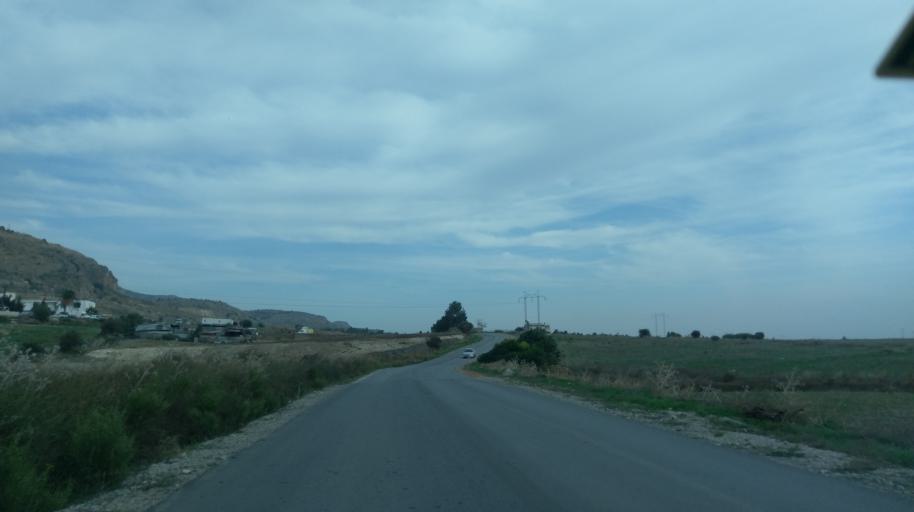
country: CY
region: Keryneia
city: Kyrenia
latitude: 35.2883
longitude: 33.2904
